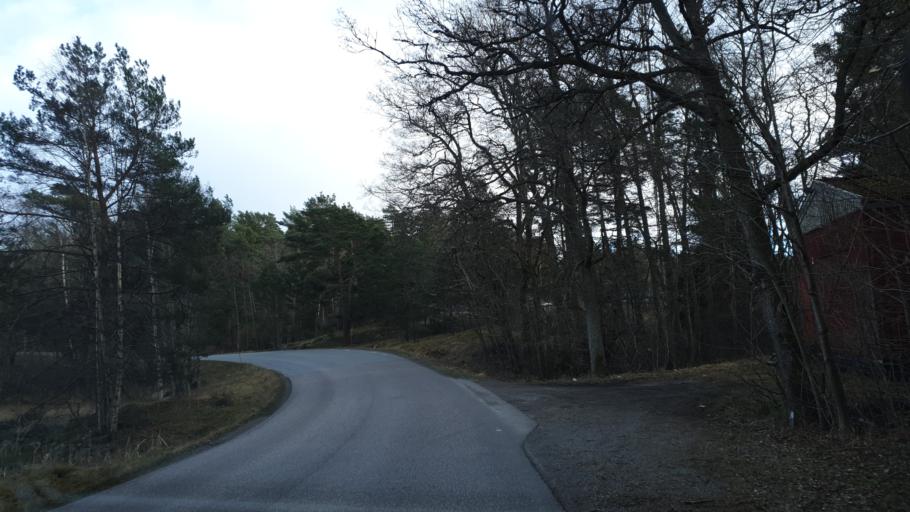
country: SE
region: Stockholm
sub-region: Varmdo Kommun
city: Holo
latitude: 59.3586
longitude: 18.6921
